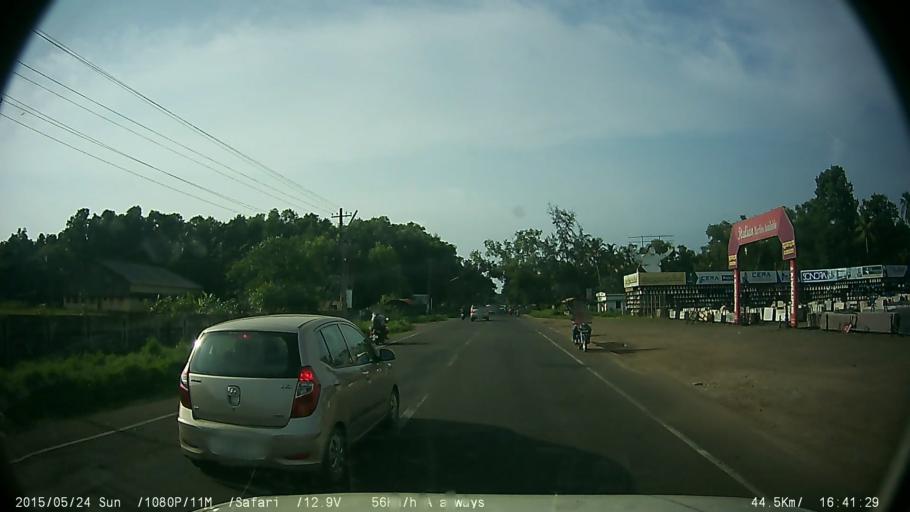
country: IN
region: Kerala
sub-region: Alappuzha
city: Shertallai
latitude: 9.6322
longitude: 76.3337
